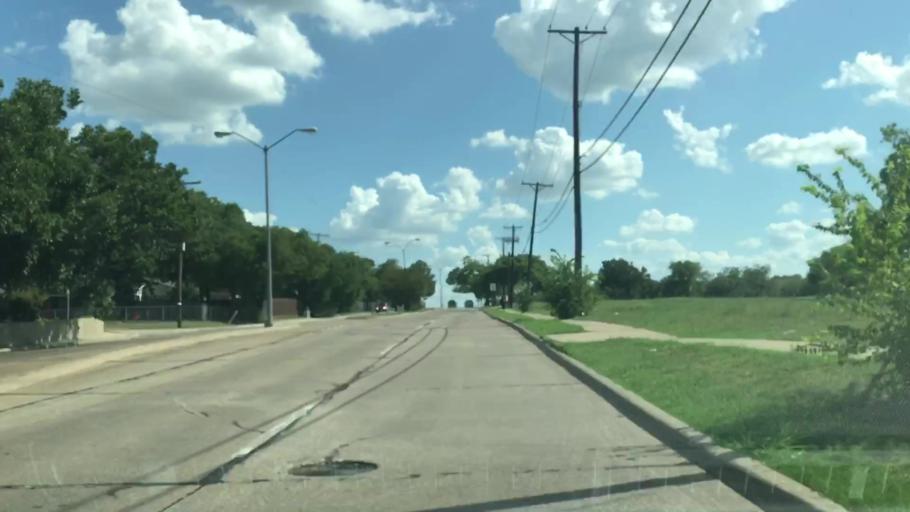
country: US
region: Texas
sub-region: Dallas County
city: Irving
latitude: 32.8543
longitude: -97.0081
